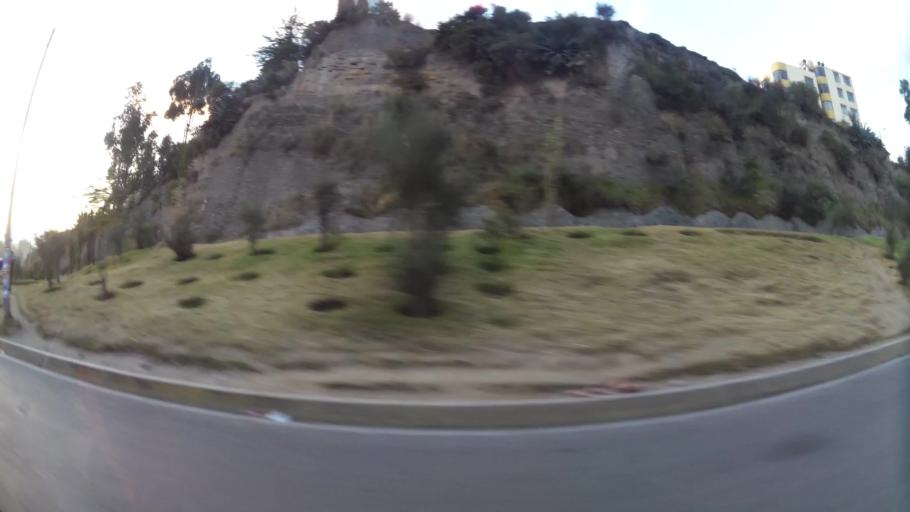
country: PE
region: Junin
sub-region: Provincia de Huancayo
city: Pilcomay
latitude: -12.0533
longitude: -75.2373
